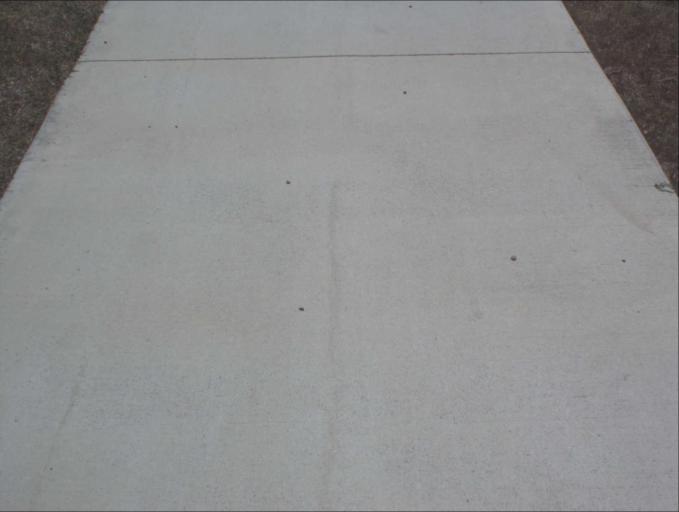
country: AU
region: Queensland
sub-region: Logan
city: Windaroo
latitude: -27.7354
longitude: 153.2011
